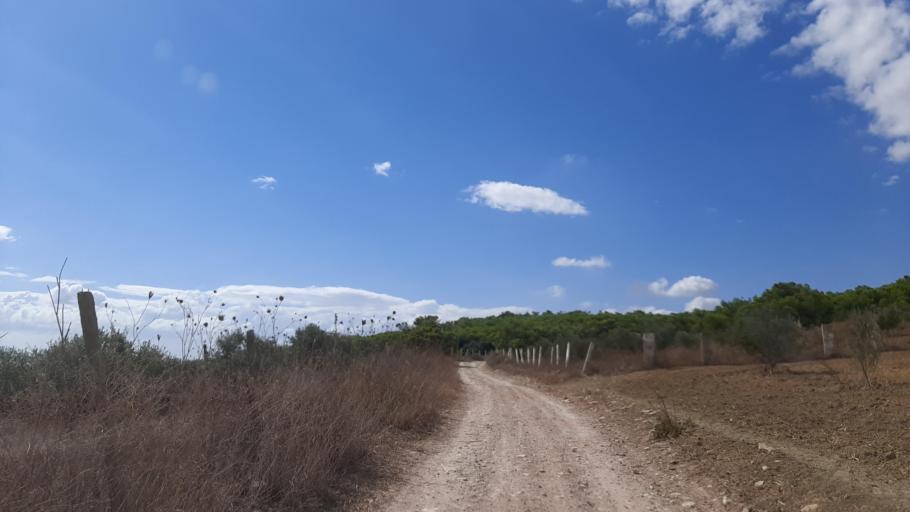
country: TN
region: Zaghwan
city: Zaghouan
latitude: 36.5114
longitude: 10.1838
